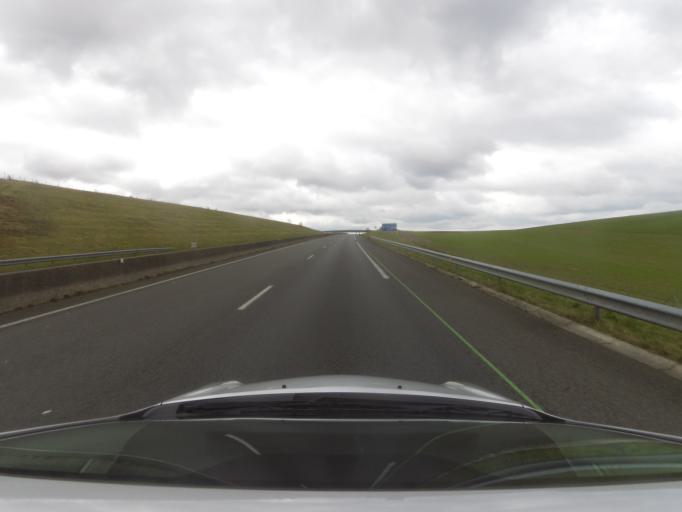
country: FR
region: Nord-Pas-de-Calais
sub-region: Departement du Pas-de-Calais
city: Neufchatel-Hardelot
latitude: 50.5989
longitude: 1.6495
